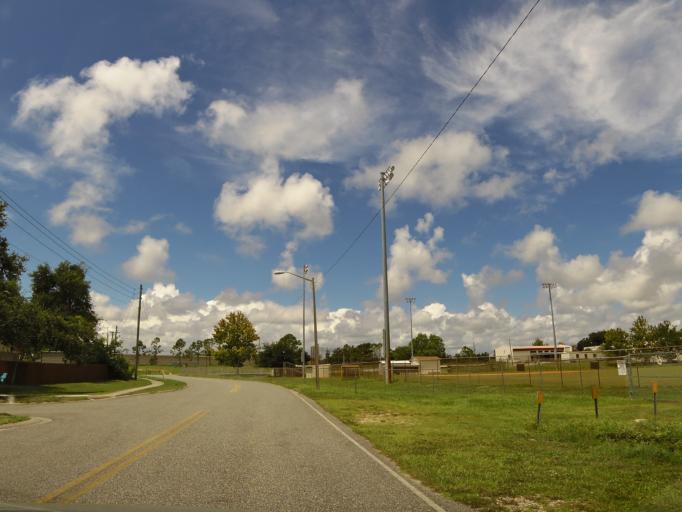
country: US
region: Florida
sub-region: Brevard County
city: Mims
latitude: 28.6229
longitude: -80.8496
